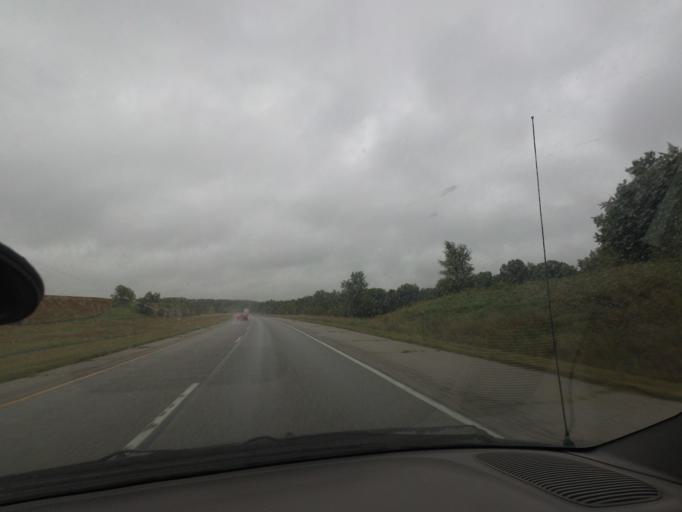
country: US
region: Illinois
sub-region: Pike County
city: Barry
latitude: 39.7266
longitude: -91.1202
